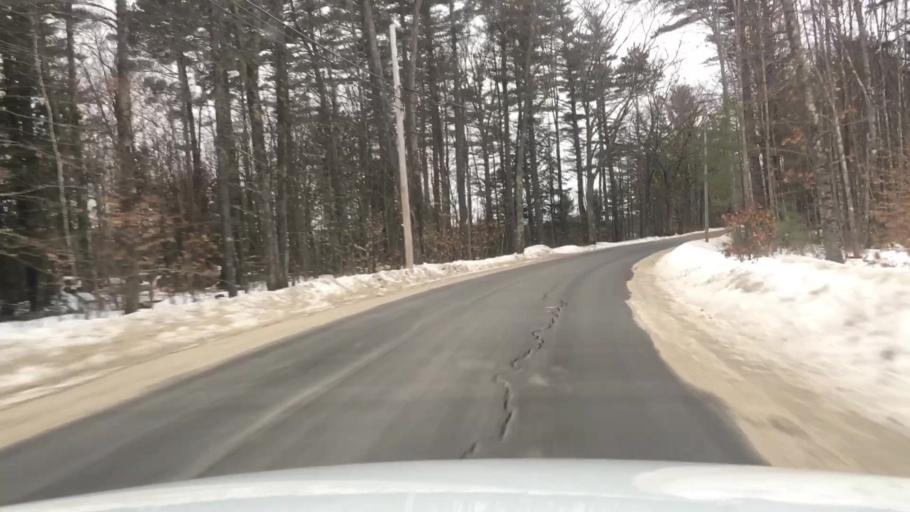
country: US
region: Maine
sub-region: York County
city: Shapleigh
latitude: 43.5257
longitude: -70.8447
